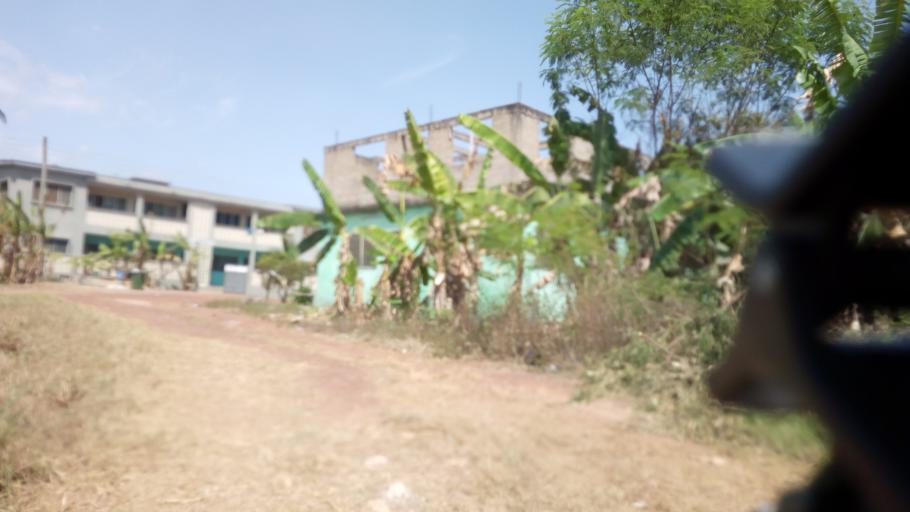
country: GH
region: Central
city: Cape Coast
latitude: 5.1317
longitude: -1.2801
